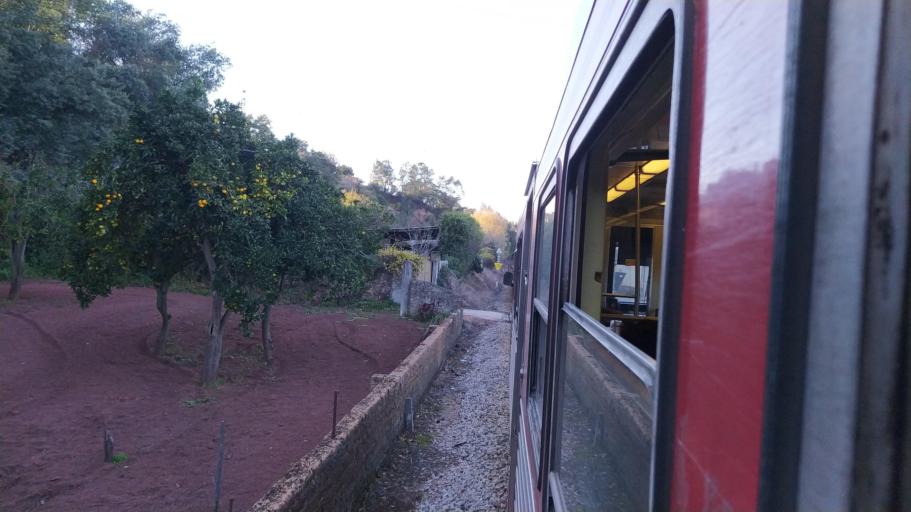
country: PT
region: Aveiro
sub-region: Aveiro
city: Eixo
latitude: 40.6126
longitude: -8.5351
